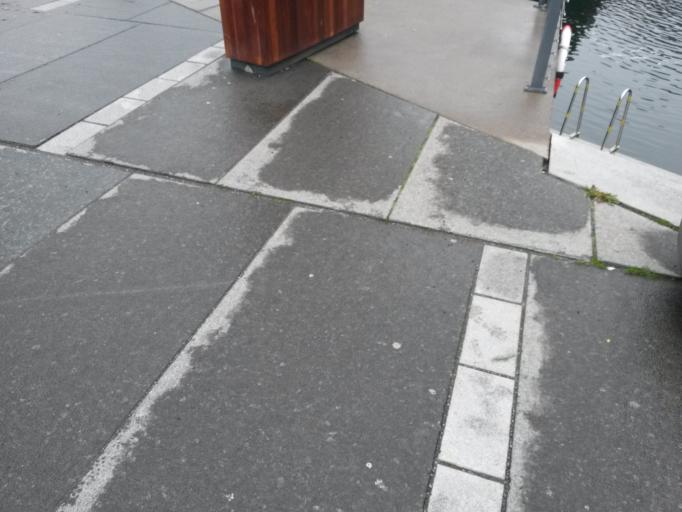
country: NO
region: Oslo
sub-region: Oslo
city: Oslo
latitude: 59.9093
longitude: 10.7235
